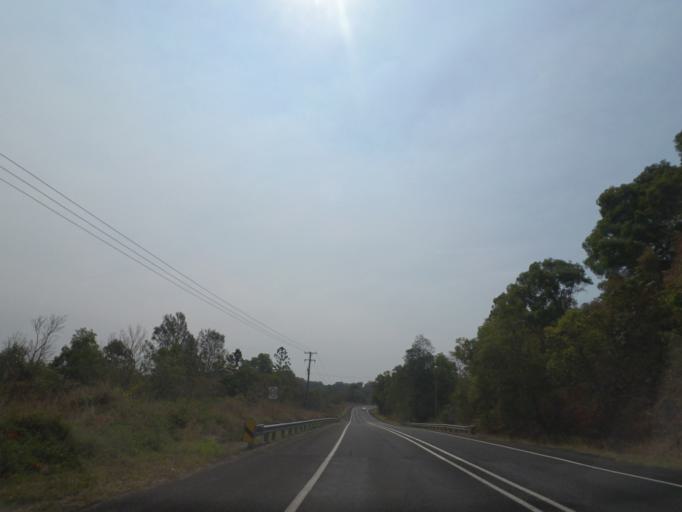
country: AU
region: New South Wales
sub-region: Byron Shire
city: Brunswick Heads
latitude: -28.5247
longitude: 153.5330
